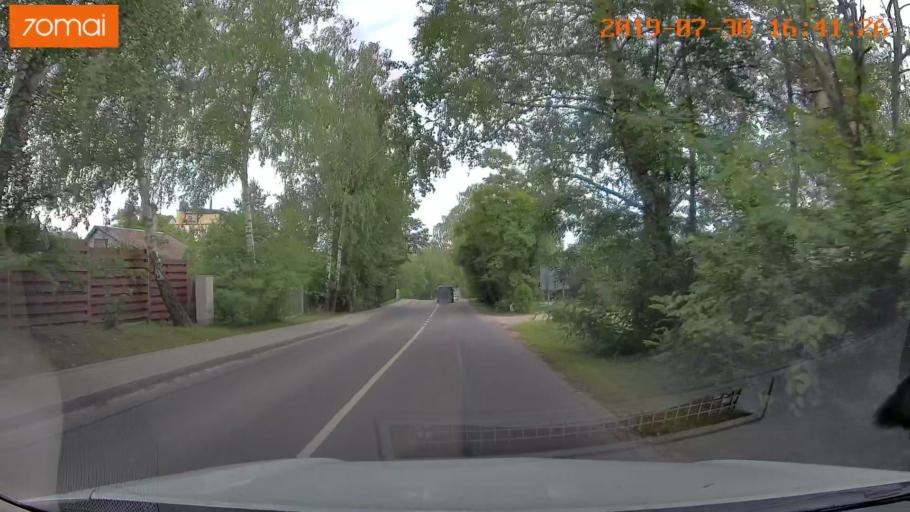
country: LT
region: Vilnius County
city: Rasos
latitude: 54.7112
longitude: 25.3557
